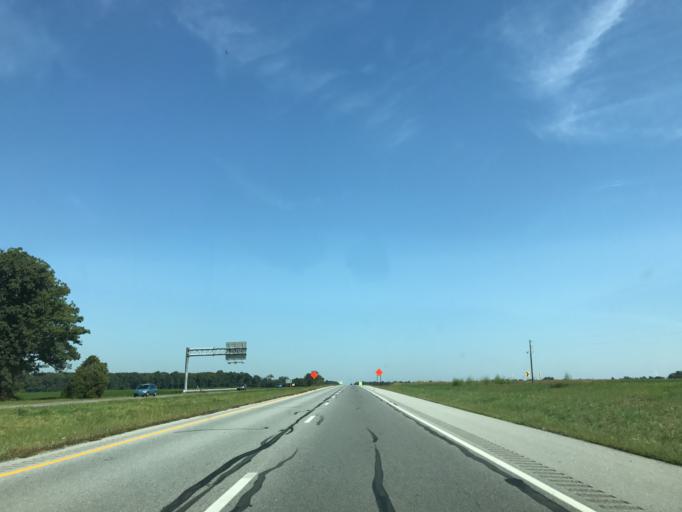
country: US
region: Delaware
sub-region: New Castle County
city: Middletown
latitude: 39.3917
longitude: -75.7918
